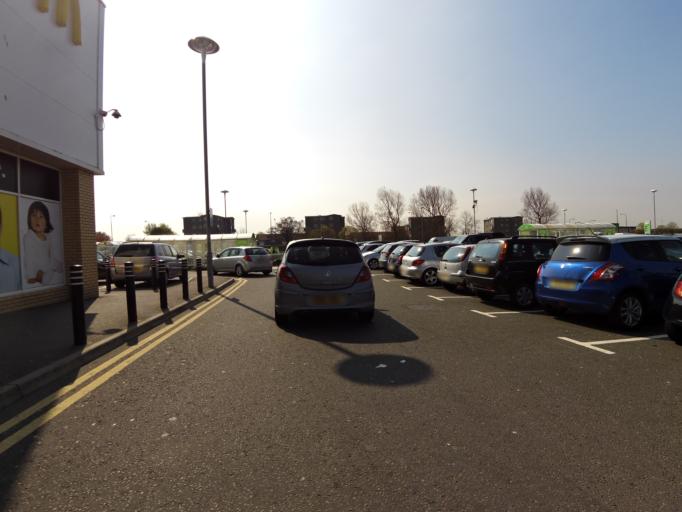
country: GB
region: Scotland
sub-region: Fife
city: Kirkcaldy
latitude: 56.1347
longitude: -3.1458
